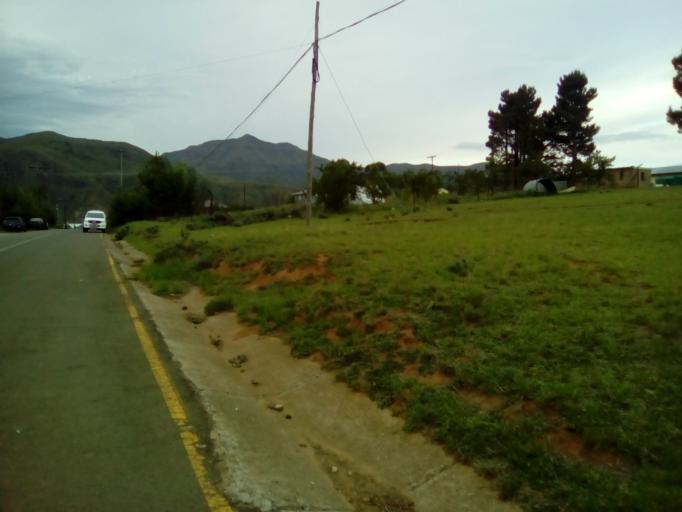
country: LS
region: Qacha's Nek
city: Qacha's Nek
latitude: -30.1095
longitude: 28.6816
